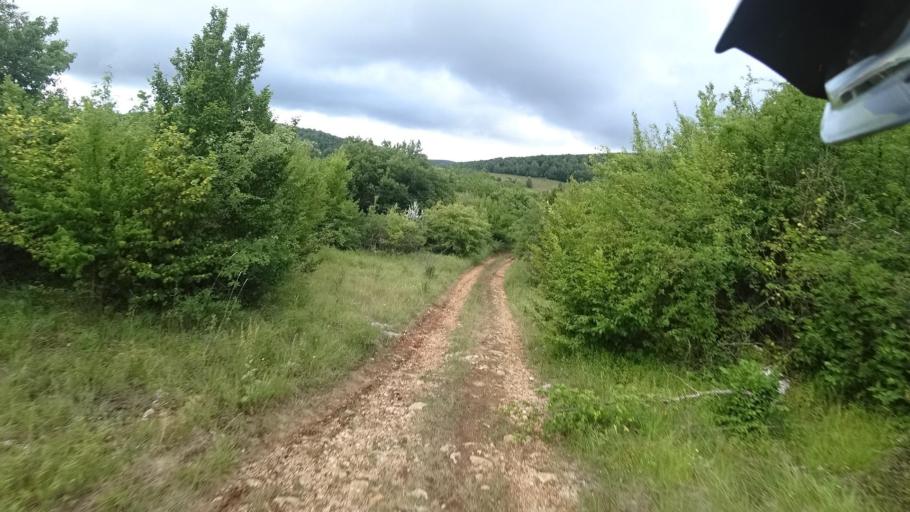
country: HR
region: Licko-Senjska
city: Jezerce
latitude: 44.7602
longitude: 15.4845
